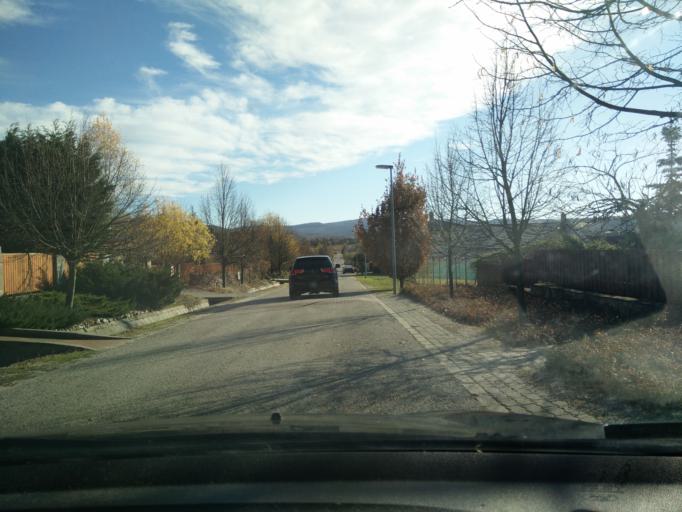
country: HU
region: Pest
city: Piliscsaba
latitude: 47.6480
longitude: 18.8166
